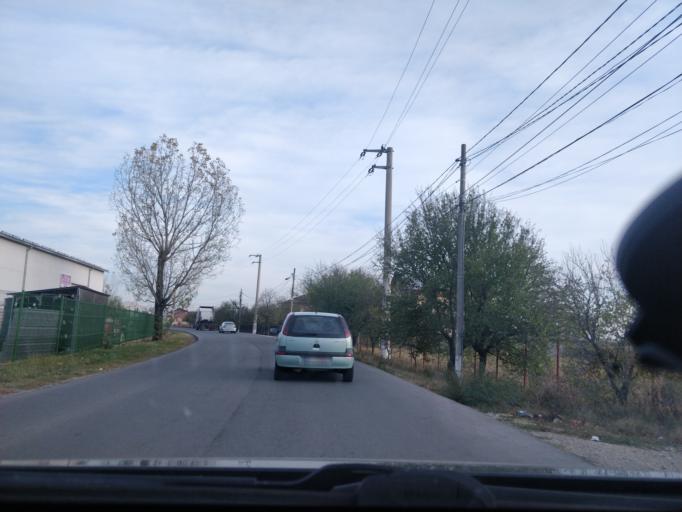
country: RO
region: Giurgiu
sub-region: Comuna Bolintin Vale
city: Malu Spart
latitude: 44.4342
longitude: 25.7232
